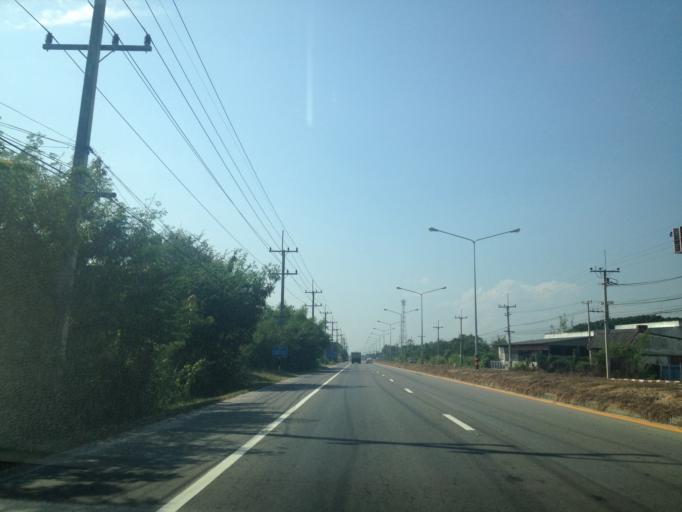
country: TH
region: Chiang Mai
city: Doi Lo
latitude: 18.5003
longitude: 98.8208
